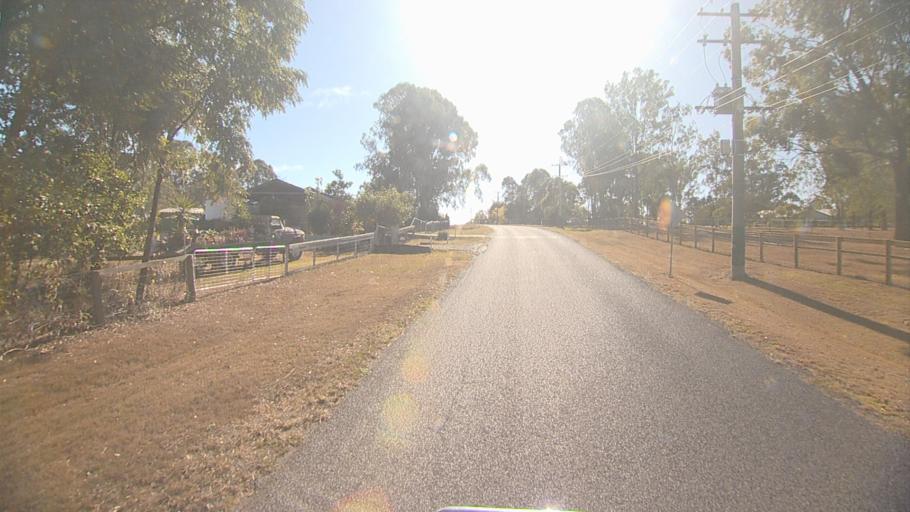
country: AU
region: Queensland
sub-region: Logan
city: Cedar Vale
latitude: -27.8667
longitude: 152.9842
